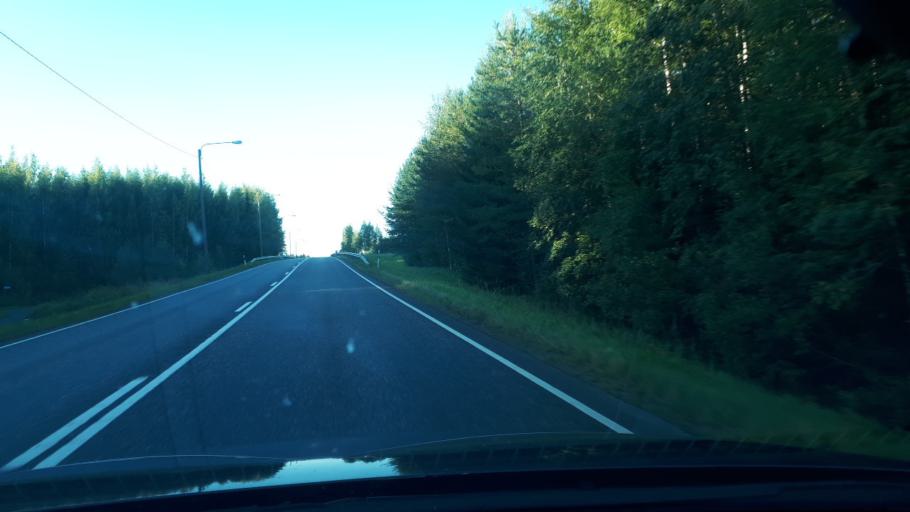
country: FI
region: Northern Savo
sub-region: Ylae-Savo
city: Lapinlahti
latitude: 63.4297
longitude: 27.3282
